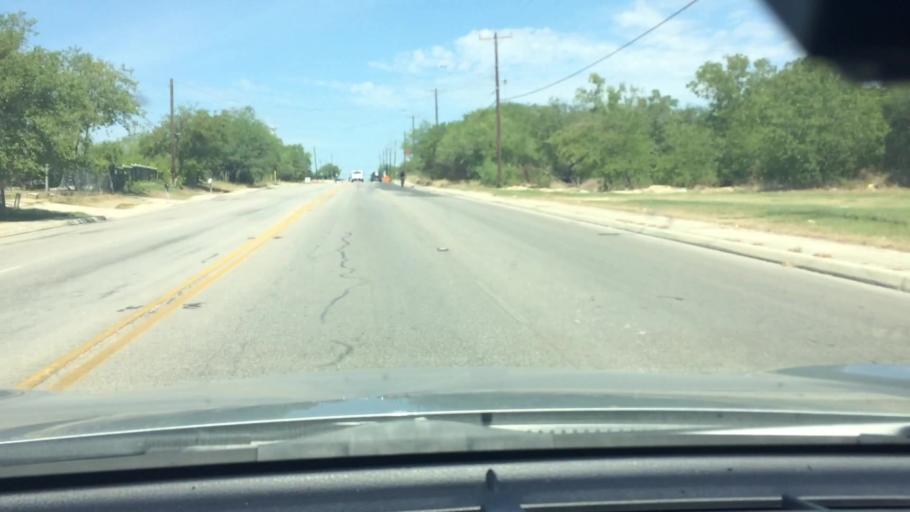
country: US
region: Texas
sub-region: Bexar County
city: San Antonio
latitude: 29.3997
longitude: -98.4389
